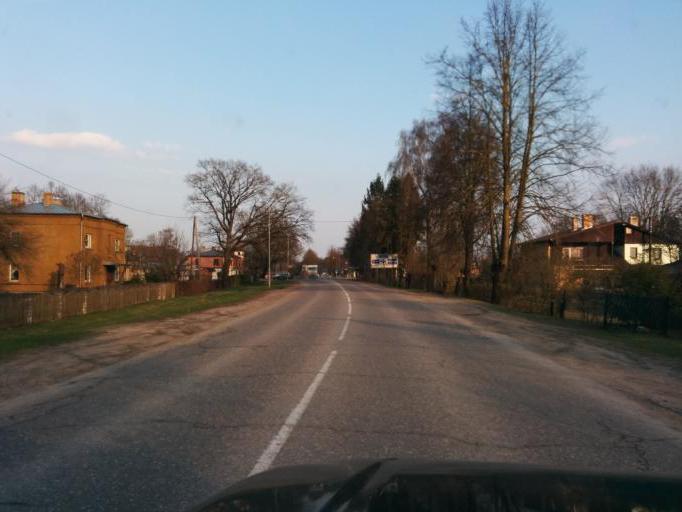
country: LV
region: Jelgava
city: Jelgava
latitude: 56.6589
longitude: 23.7400
